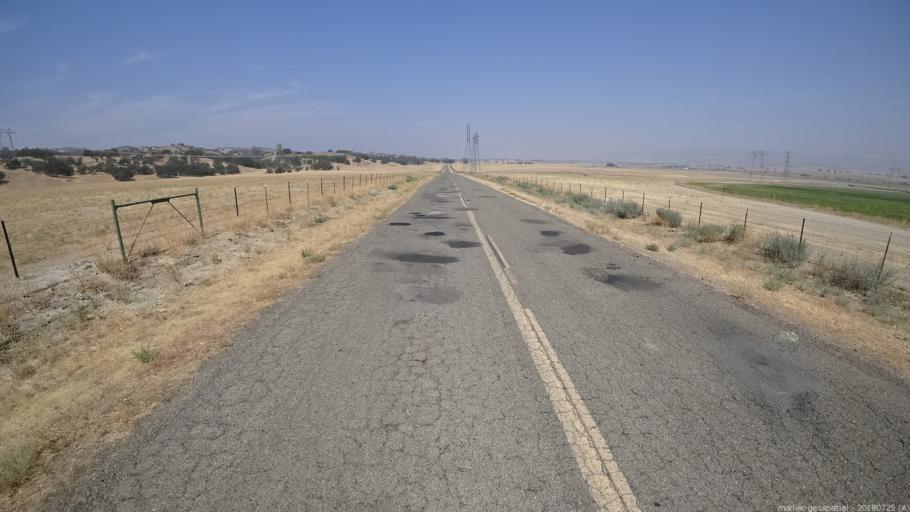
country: US
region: California
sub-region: San Luis Obispo County
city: Shandon
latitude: 35.8163
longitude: -120.3777
